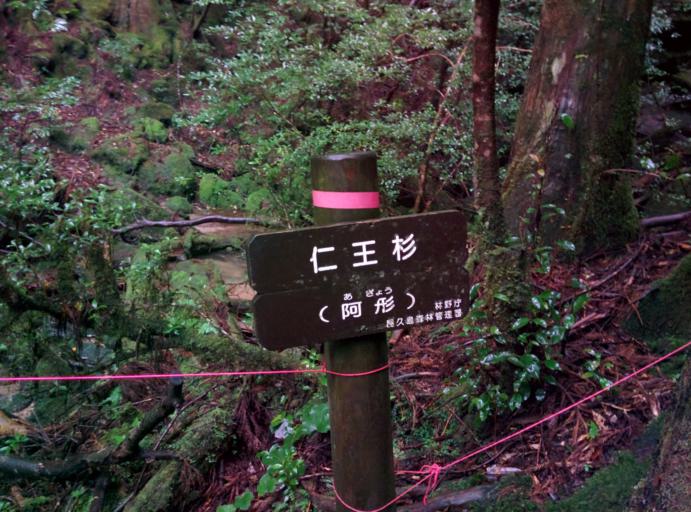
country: JP
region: Kagoshima
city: Nishinoomote
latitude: 30.3532
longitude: 130.5455
